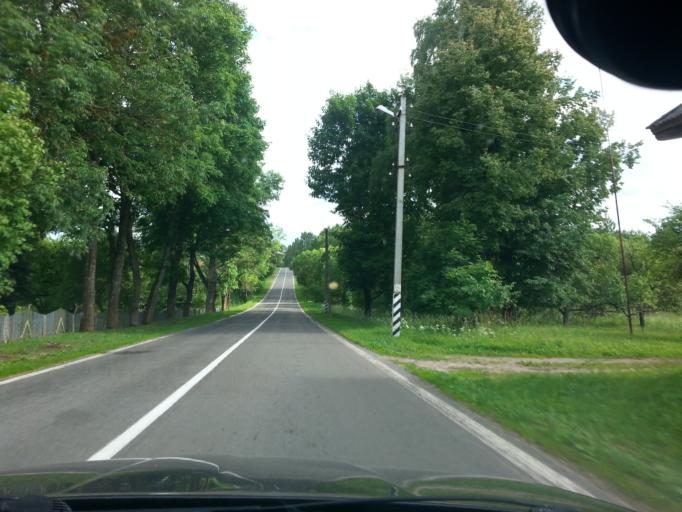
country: BY
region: Minsk
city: Svir
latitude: 54.8991
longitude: 26.3865
